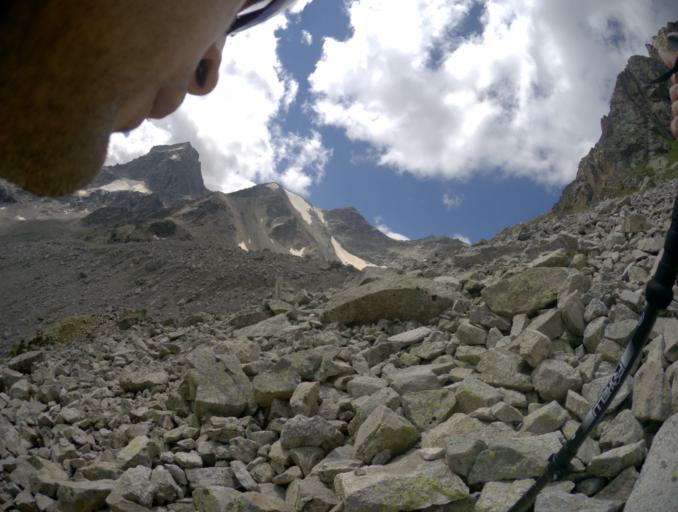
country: RU
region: Karachayevo-Cherkesiya
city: Uchkulan
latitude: 43.3251
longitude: 42.0896
